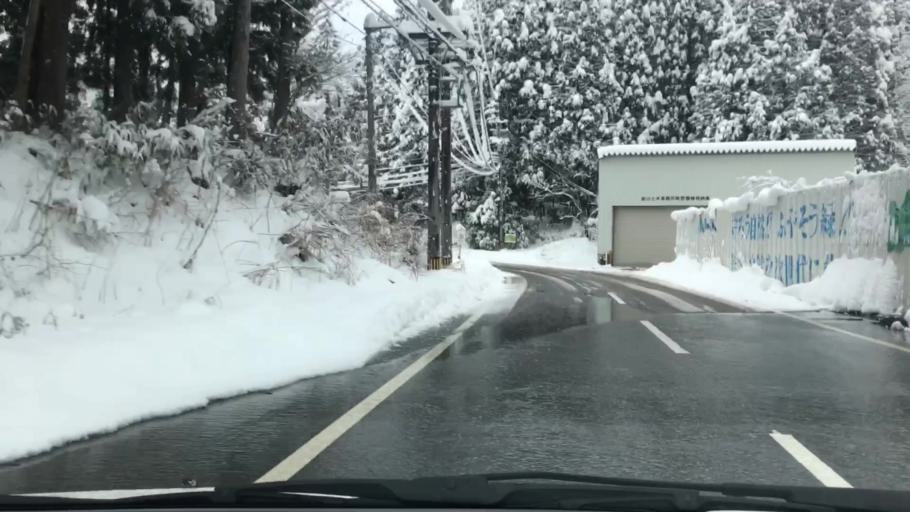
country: JP
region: Toyama
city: Kamiichi
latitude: 36.5748
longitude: 137.4092
